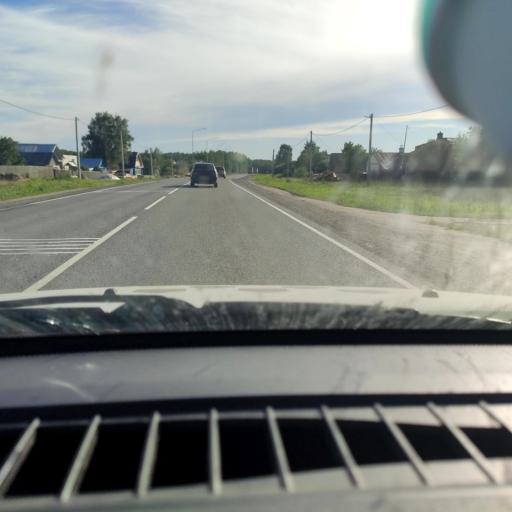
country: RU
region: Kirov
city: Vakhrushi
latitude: 58.6707
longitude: 49.9415
